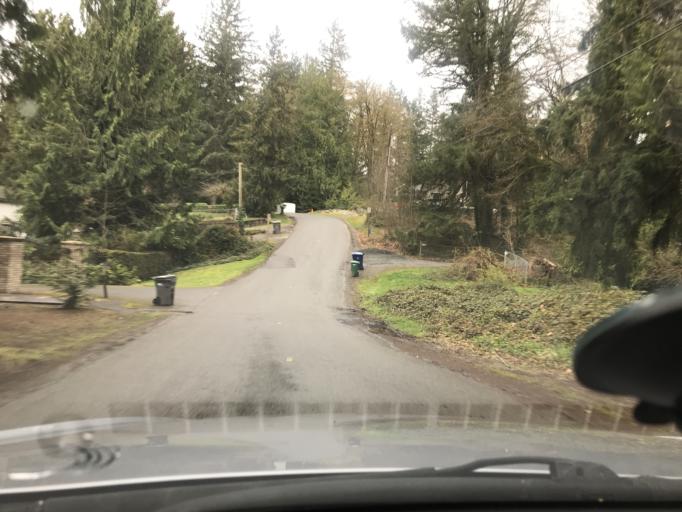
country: US
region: Washington
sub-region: King County
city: Ames Lake
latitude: 47.6448
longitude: -121.9580
